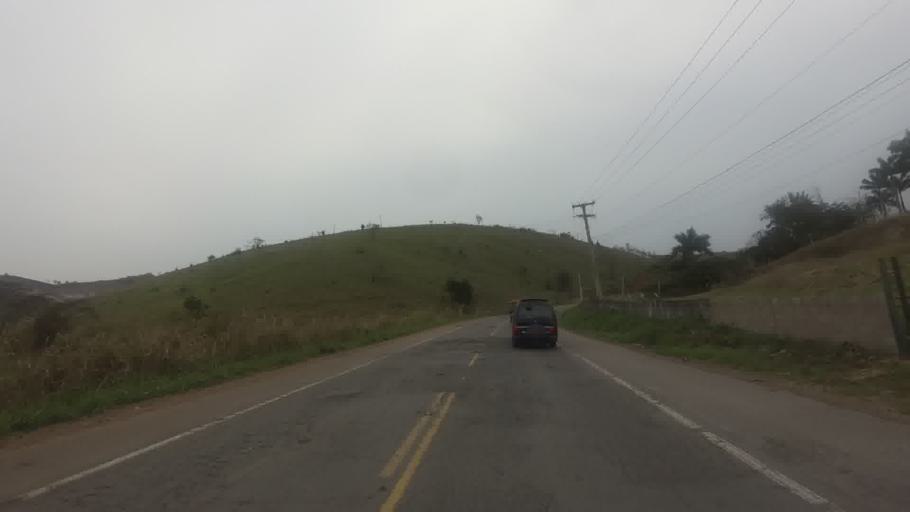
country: BR
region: Rio de Janeiro
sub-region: Santo Antonio De Padua
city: Santo Antonio de Padua
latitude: -21.6038
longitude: -42.2408
